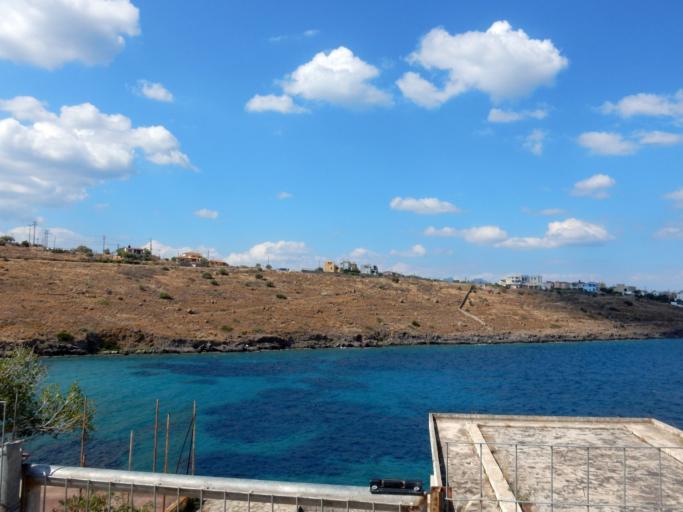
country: GR
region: Attica
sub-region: Nomos Piraios
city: Aegina
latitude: 37.6961
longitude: 23.4642
